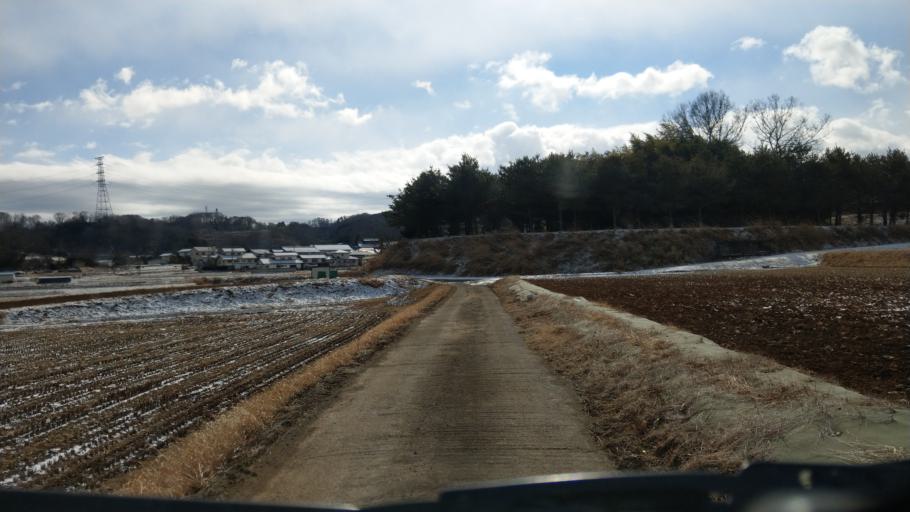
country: JP
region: Nagano
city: Kamimaruko
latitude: 36.2768
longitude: 138.3360
